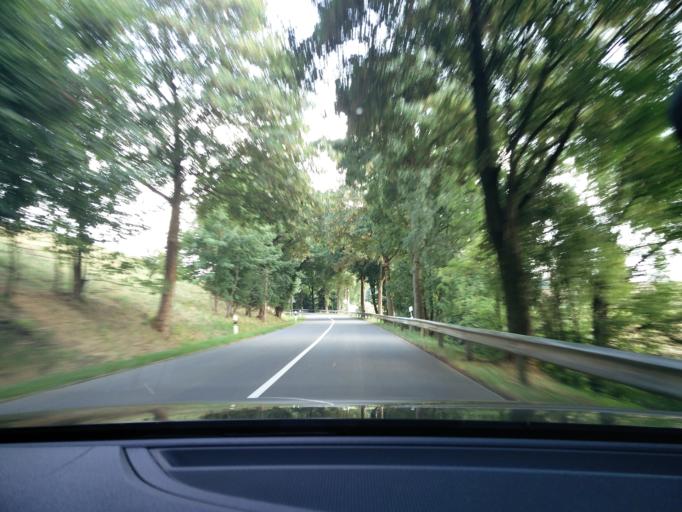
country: DE
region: North Rhine-Westphalia
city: Lichtenau
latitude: 51.6789
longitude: 8.9113
